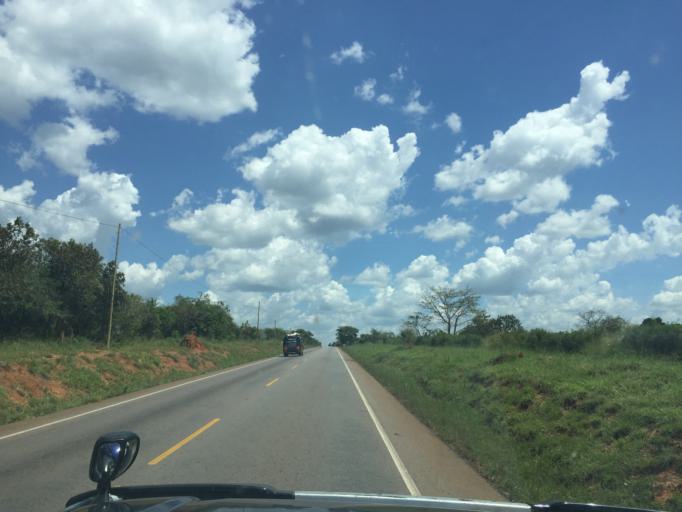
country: UG
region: Central Region
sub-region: Nakasongola District
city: Nakasongola
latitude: 1.3442
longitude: 32.3922
